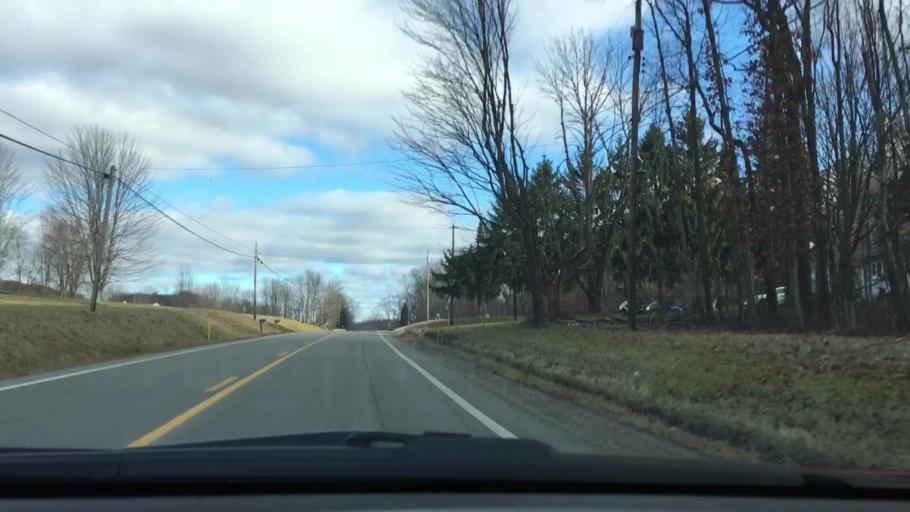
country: US
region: Pennsylvania
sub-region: Westmoreland County
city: Avonmore
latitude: 40.6148
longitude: -79.4351
